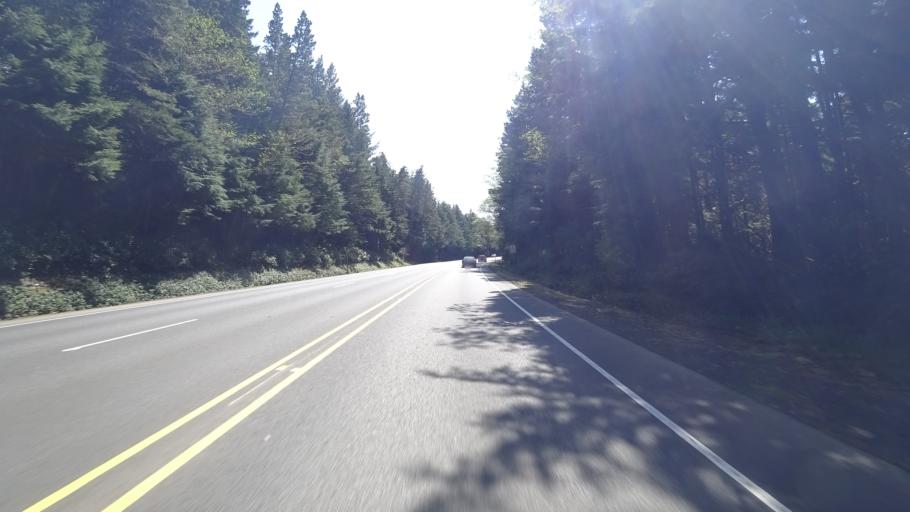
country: US
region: Oregon
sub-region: Lincoln County
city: Depoe Bay
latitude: 44.7470
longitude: -124.0516
